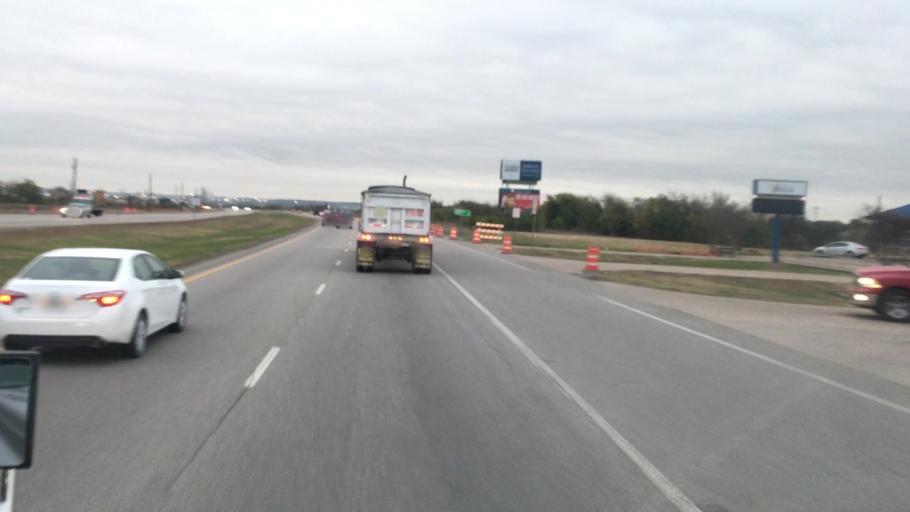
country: US
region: Texas
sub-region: Johnson County
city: Venus
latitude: 32.4358
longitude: -97.1038
